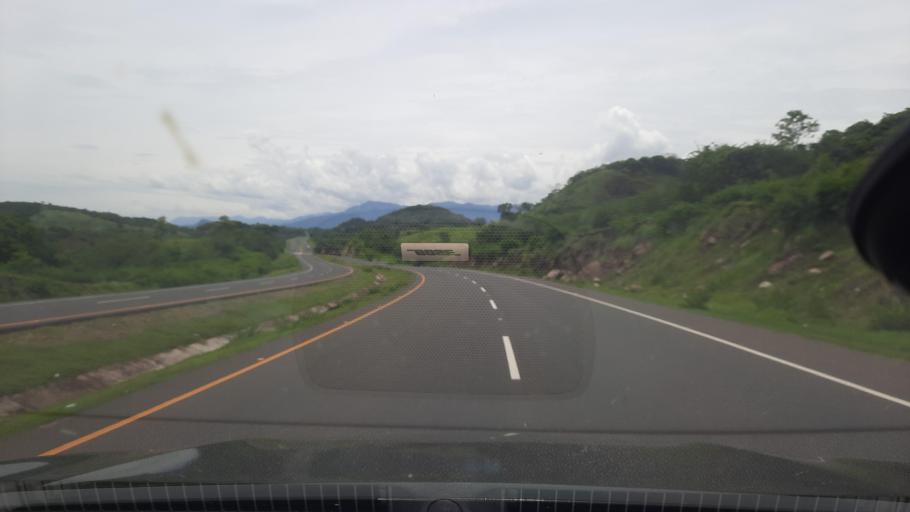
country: HN
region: Valle
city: Aramecina
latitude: 13.6690
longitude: -87.7350
